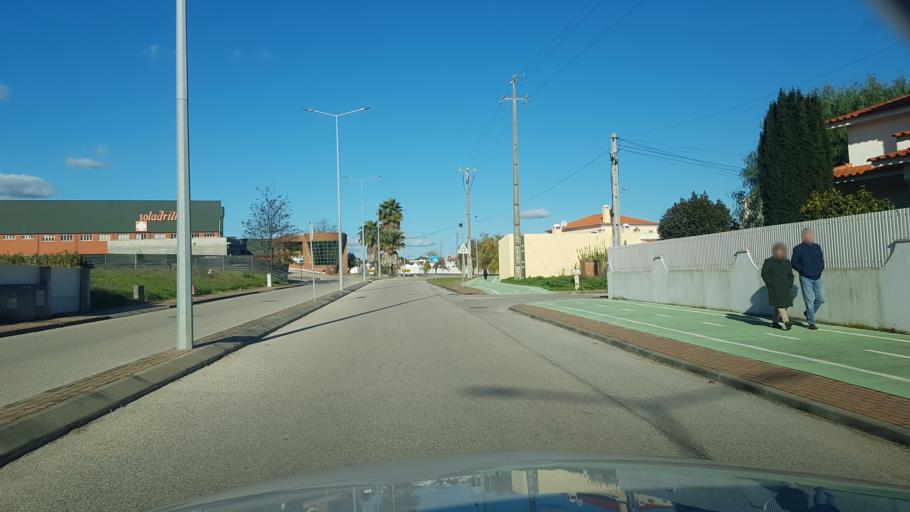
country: PT
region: Santarem
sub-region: Entroncamento
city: Entroncamento
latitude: 39.4807
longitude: -8.4725
